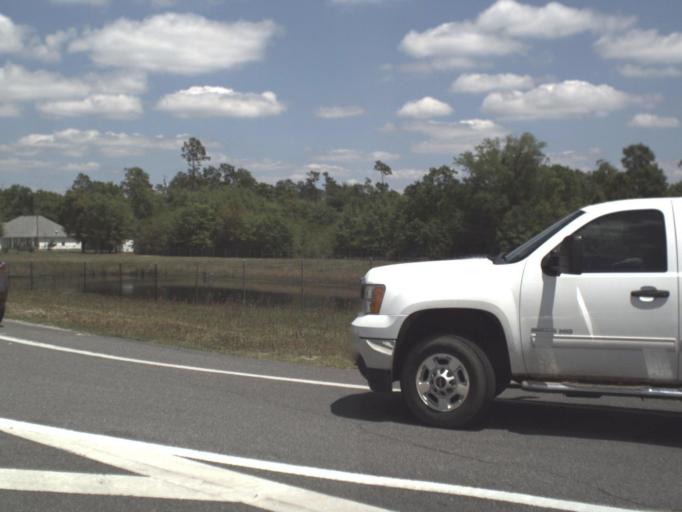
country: US
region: Florida
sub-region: Santa Rosa County
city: Point Baker
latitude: 30.7067
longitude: -87.0483
